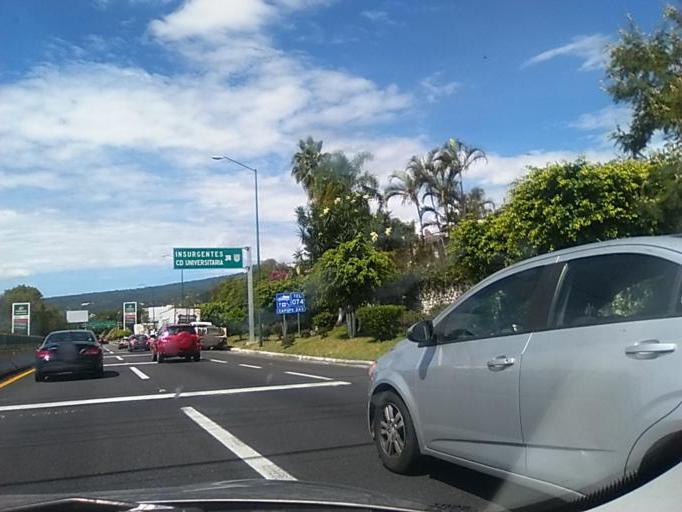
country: MX
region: Morelos
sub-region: Cuernavaca
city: Fraccionamiento Lomas de Ahuatlan
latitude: 18.9741
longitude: -99.2352
